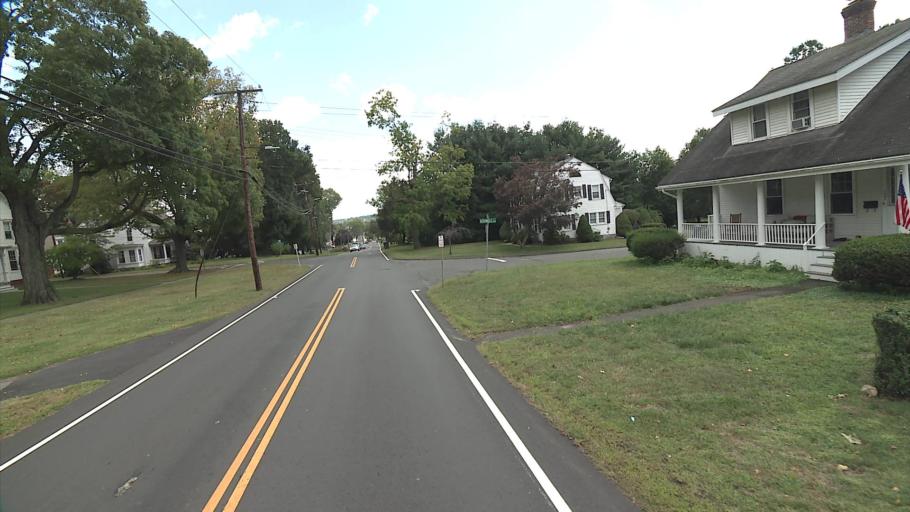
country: US
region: Connecticut
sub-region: Hartford County
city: Wethersfield
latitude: 41.6644
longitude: -72.6436
